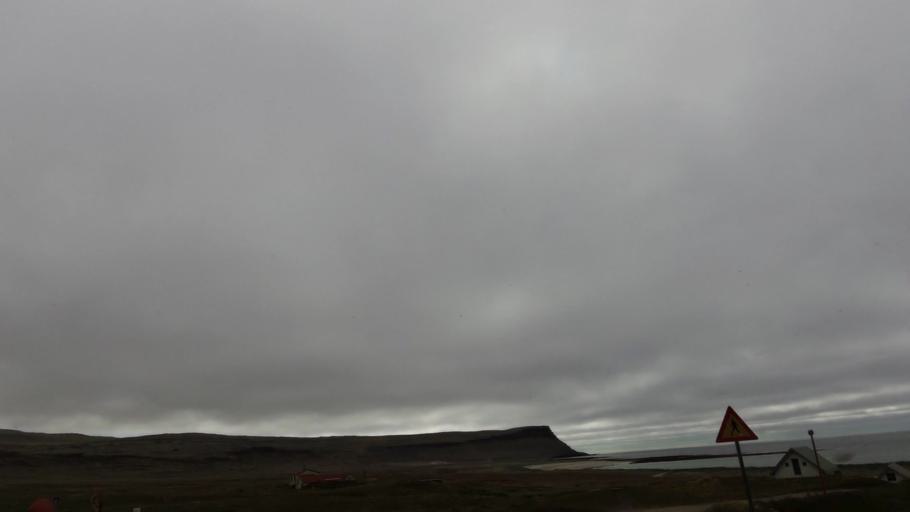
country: IS
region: West
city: Olafsvik
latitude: 65.5283
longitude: -24.4563
